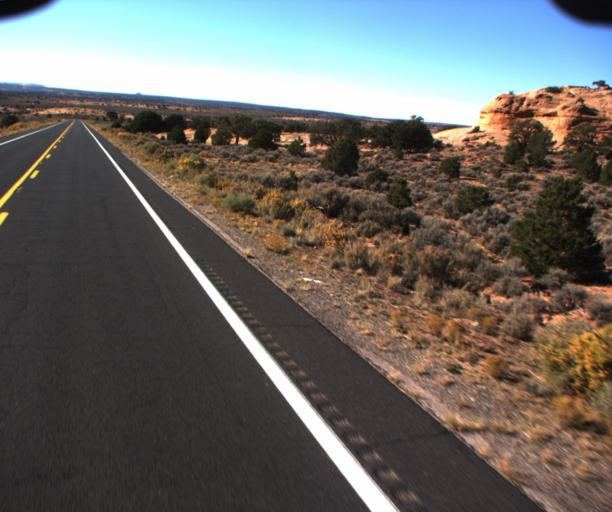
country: US
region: Arizona
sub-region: Coconino County
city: Kaibito
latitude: 36.5628
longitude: -110.7305
